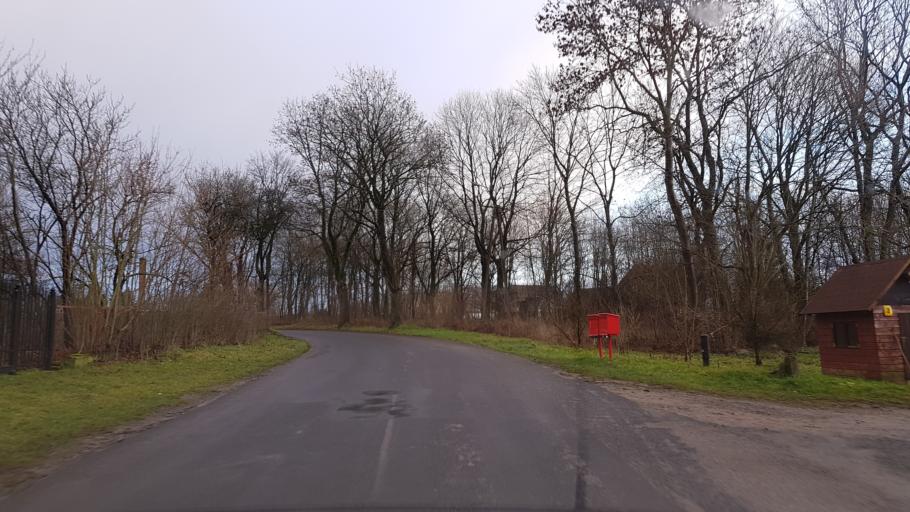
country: PL
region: West Pomeranian Voivodeship
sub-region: Powiat swidwinski
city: Rabino
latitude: 53.9465
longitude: 15.9182
